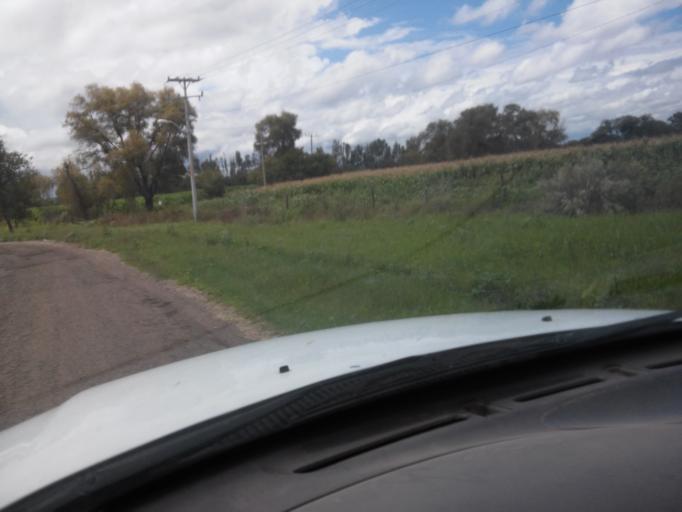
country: MX
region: Durango
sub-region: Durango
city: Jose Refugio Salcido
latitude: 24.0209
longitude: -104.5464
